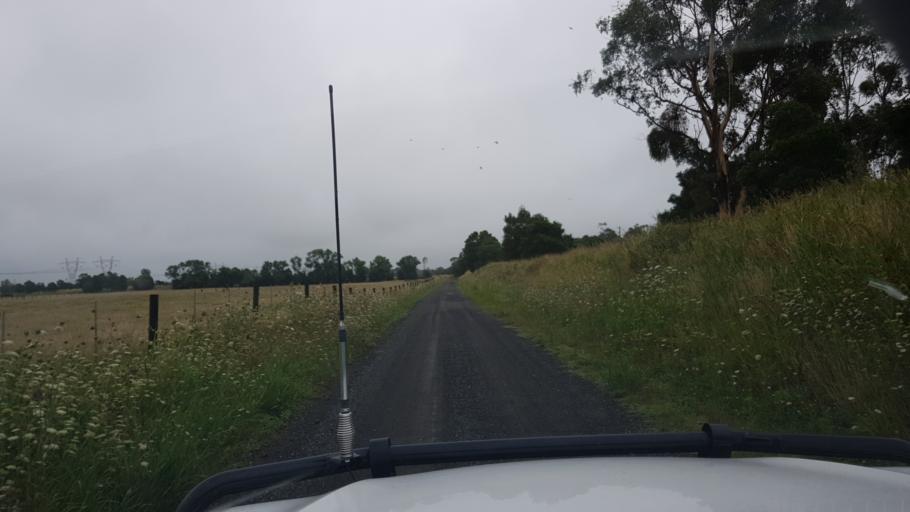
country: AU
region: Victoria
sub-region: Latrobe
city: Moe
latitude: -38.1844
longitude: 146.1166
